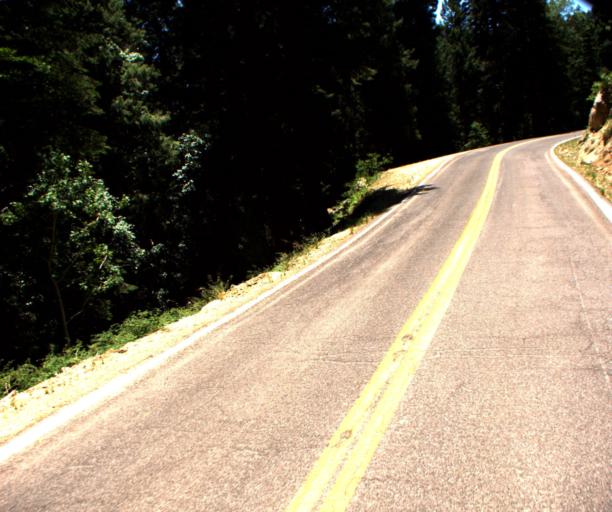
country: US
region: Arizona
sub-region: Graham County
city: Swift Trail Junction
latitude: 32.6284
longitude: -109.8269
